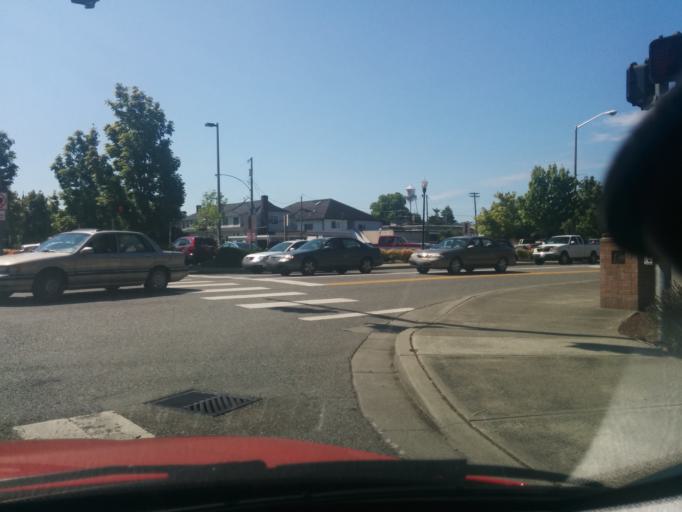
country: US
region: Washington
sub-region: Skagit County
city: Mount Vernon
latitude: 48.4177
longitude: -122.3362
